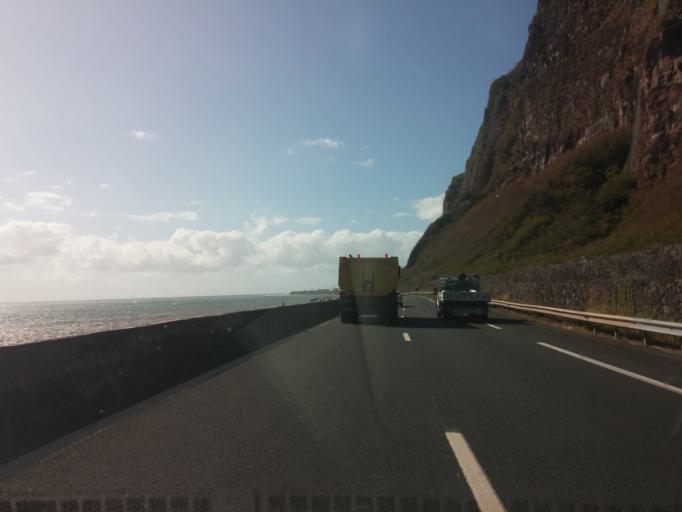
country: RE
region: Reunion
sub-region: Reunion
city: Saint-Denis
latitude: -20.8745
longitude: 55.4227
